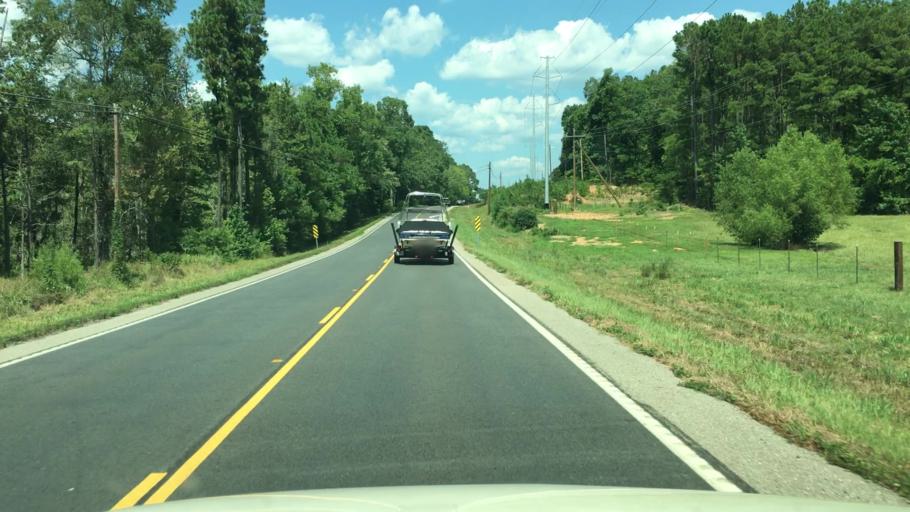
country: US
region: Arkansas
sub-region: Garland County
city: Lake Hamilton
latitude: 34.3998
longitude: -93.0996
